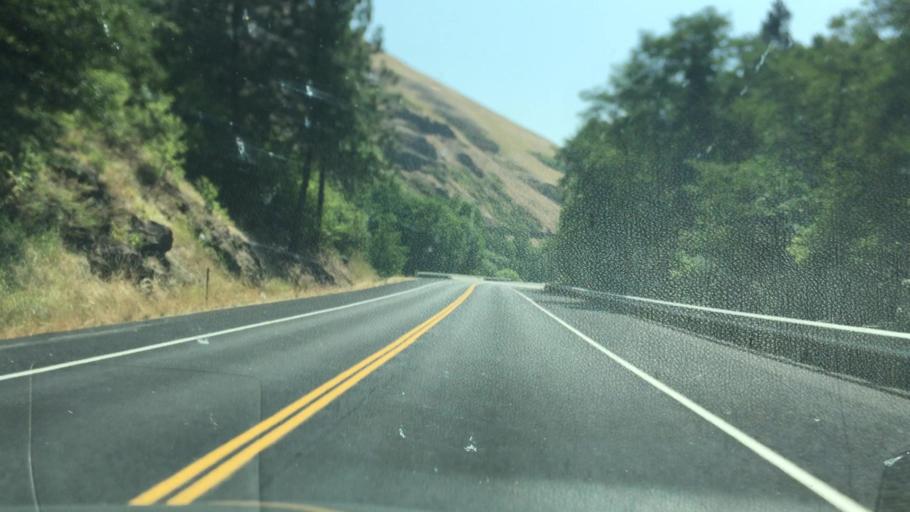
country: US
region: Idaho
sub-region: Nez Perce County
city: Lapwai
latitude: 46.3547
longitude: -116.6257
